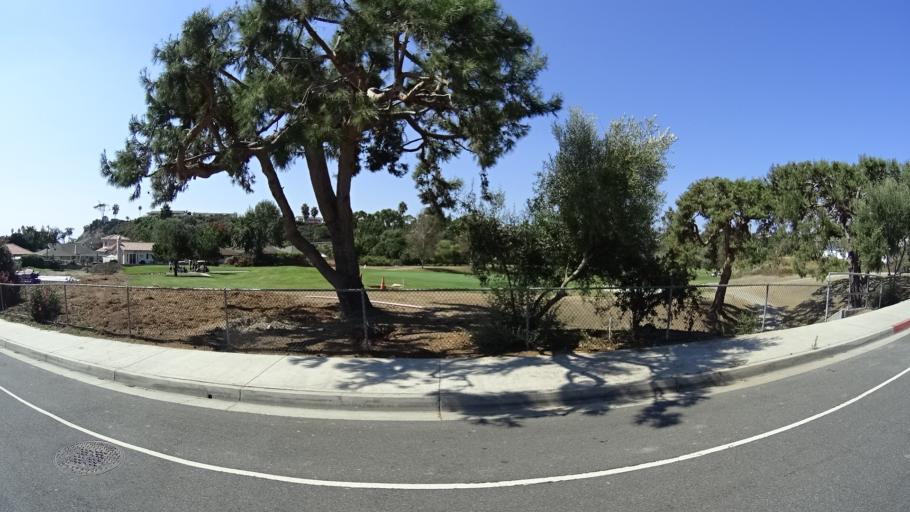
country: US
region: California
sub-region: Orange County
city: San Clemente
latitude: 33.4466
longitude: -117.6429
